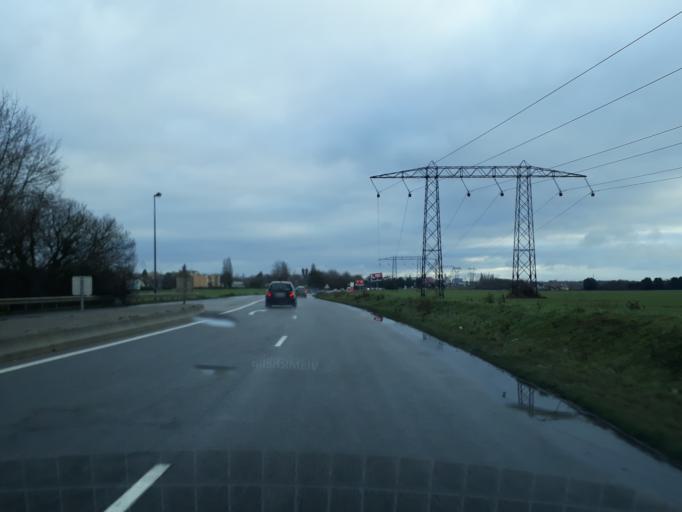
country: FR
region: Ile-de-France
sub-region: Departement de l'Essonne
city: Les Ulis
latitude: 48.6731
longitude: 2.1549
